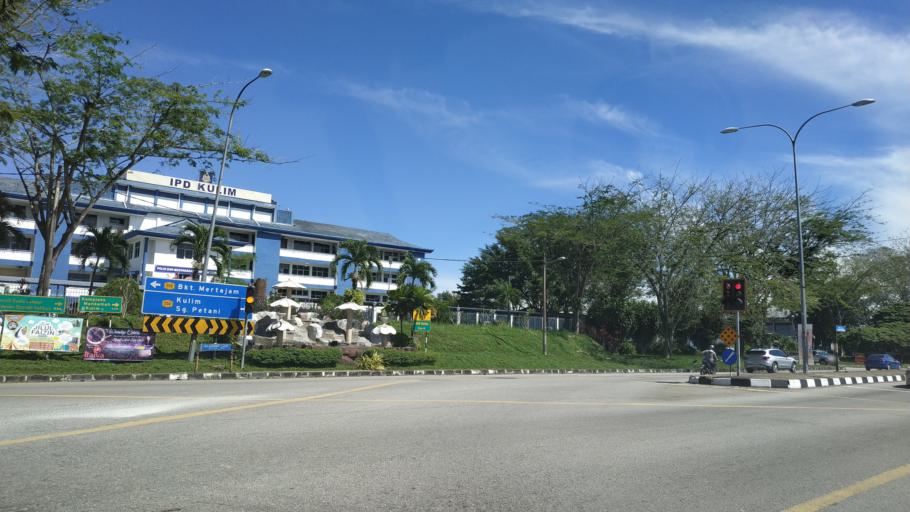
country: MY
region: Kedah
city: Kulim
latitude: 5.3550
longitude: 100.5378
